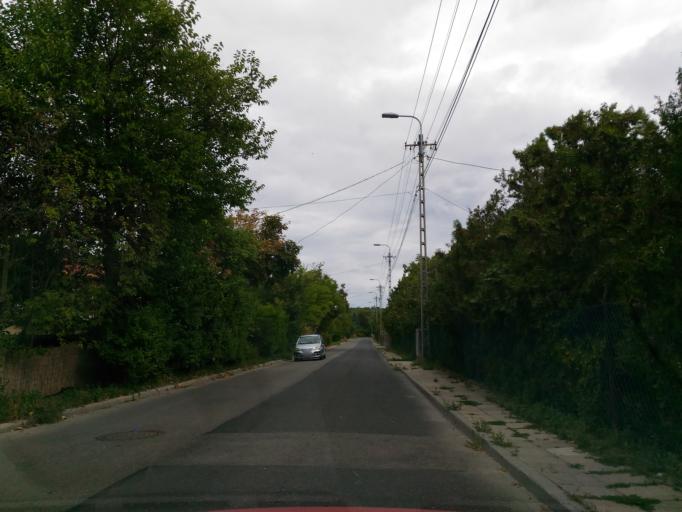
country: HU
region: Pest
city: Diosd
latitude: 47.4036
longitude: 18.9761
